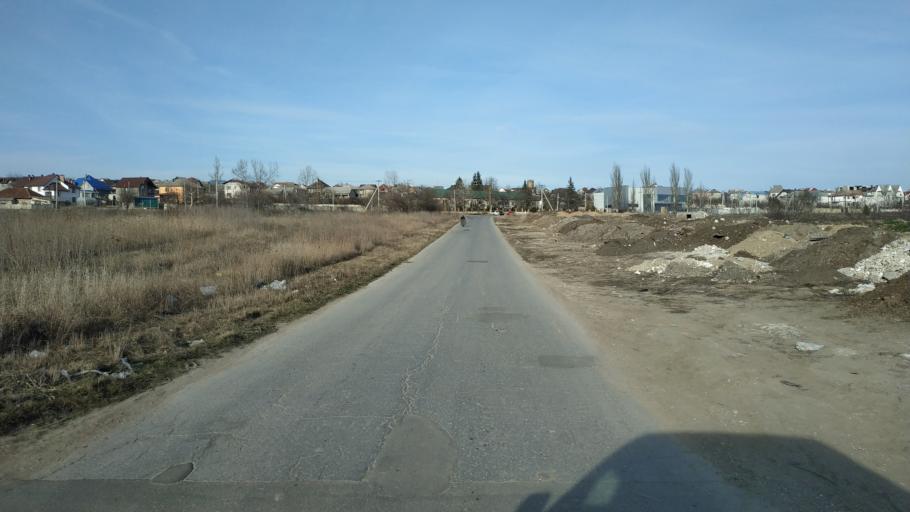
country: MD
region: Chisinau
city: Vatra
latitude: 47.0707
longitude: 28.6964
